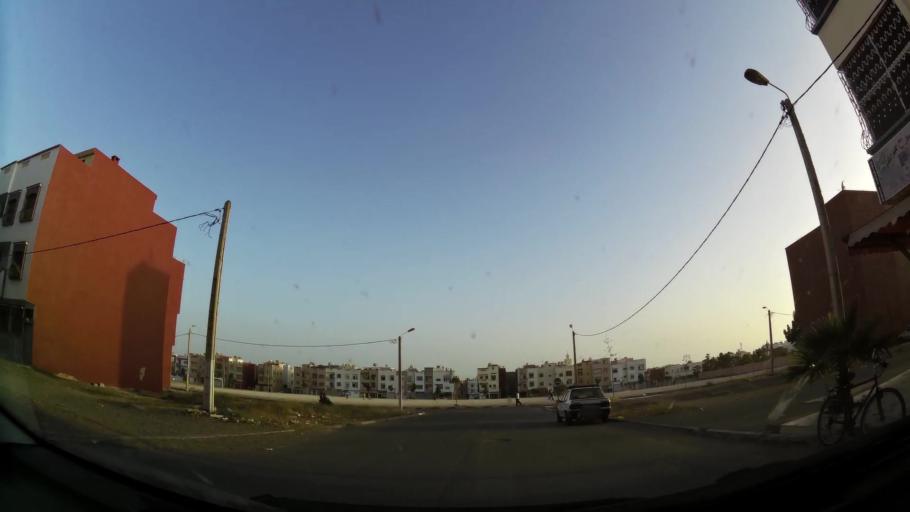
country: MA
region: Oued ed Dahab-Lagouira
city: Dakhla
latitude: 30.3959
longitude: -9.5618
